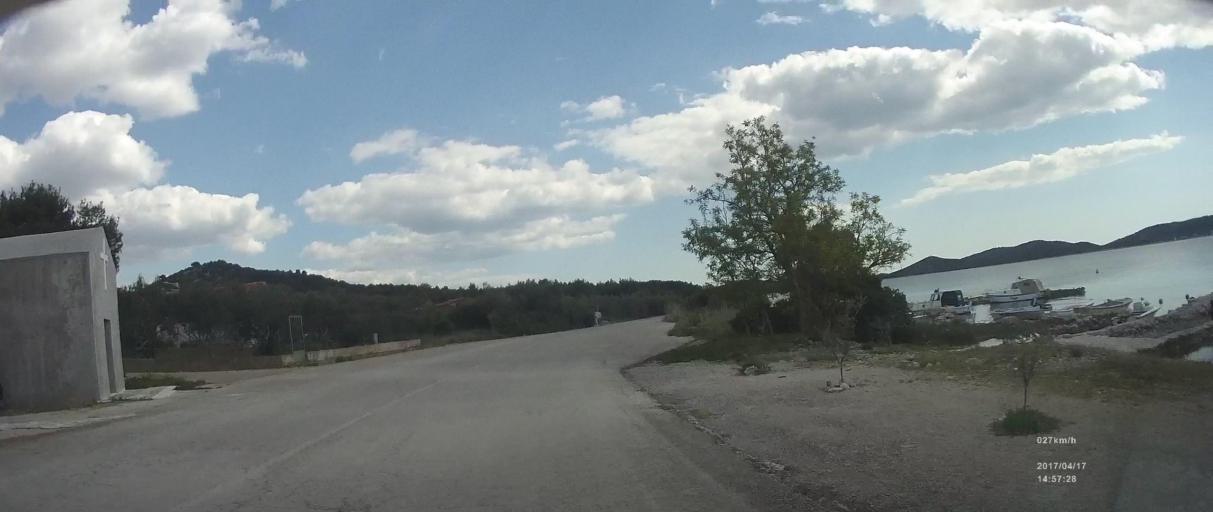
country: HR
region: Sibensko-Kniniska
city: Murter
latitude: 43.8436
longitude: 15.6252
